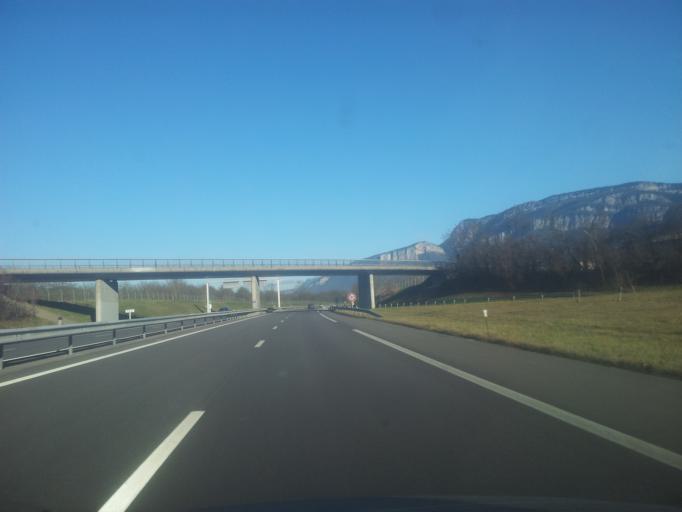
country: FR
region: Rhone-Alpes
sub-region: Departement de l'Isere
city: Vinay
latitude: 45.1987
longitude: 5.4237
